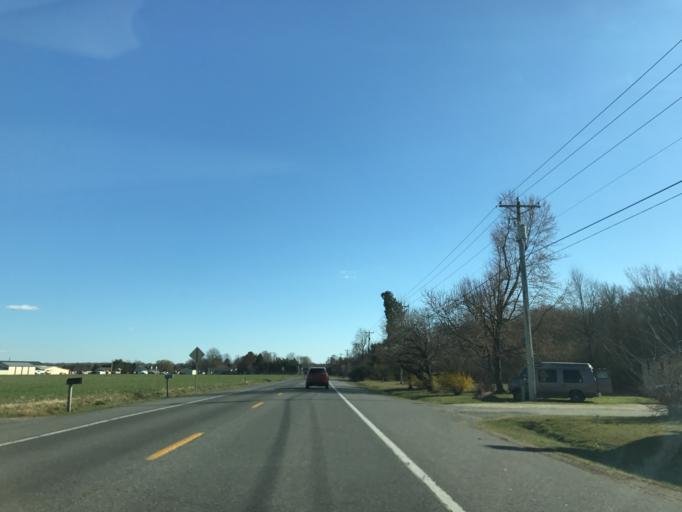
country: US
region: Maryland
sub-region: Caroline County
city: Greensboro
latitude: 39.1505
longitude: -75.8661
